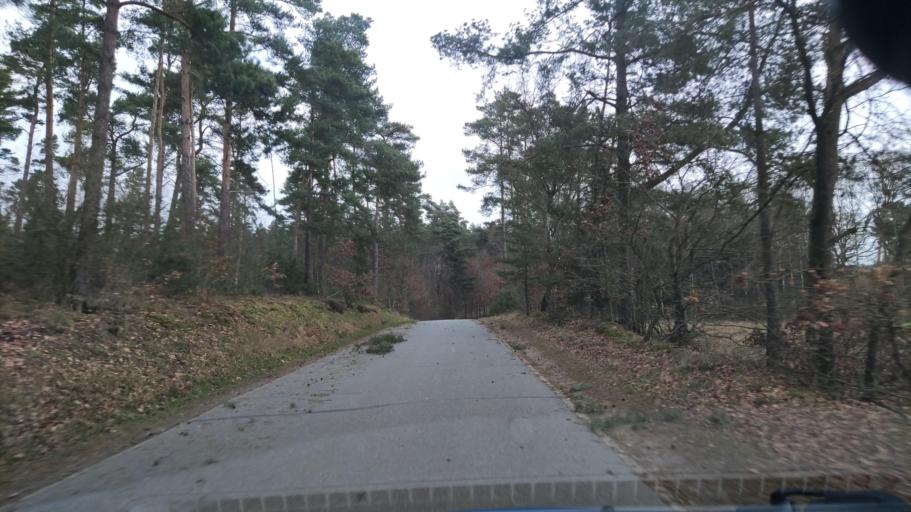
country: DE
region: Lower Saxony
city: Sudergellersen
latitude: 53.2089
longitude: 10.3216
